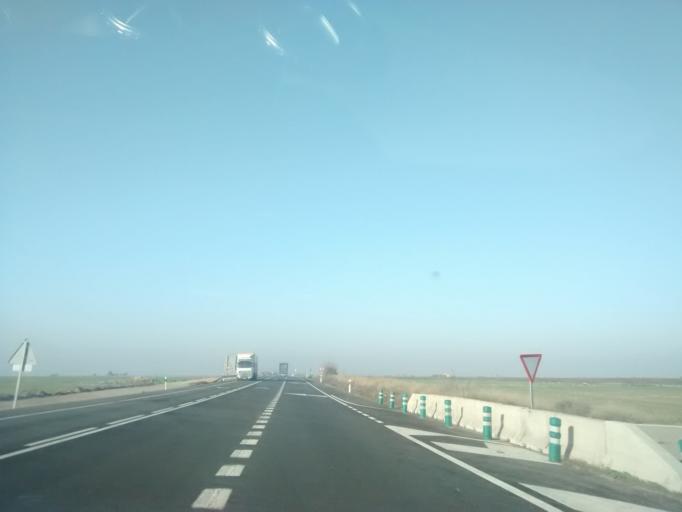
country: ES
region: Aragon
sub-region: Provincia de Huesca
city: Fraga
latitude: 41.5147
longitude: 0.2664
